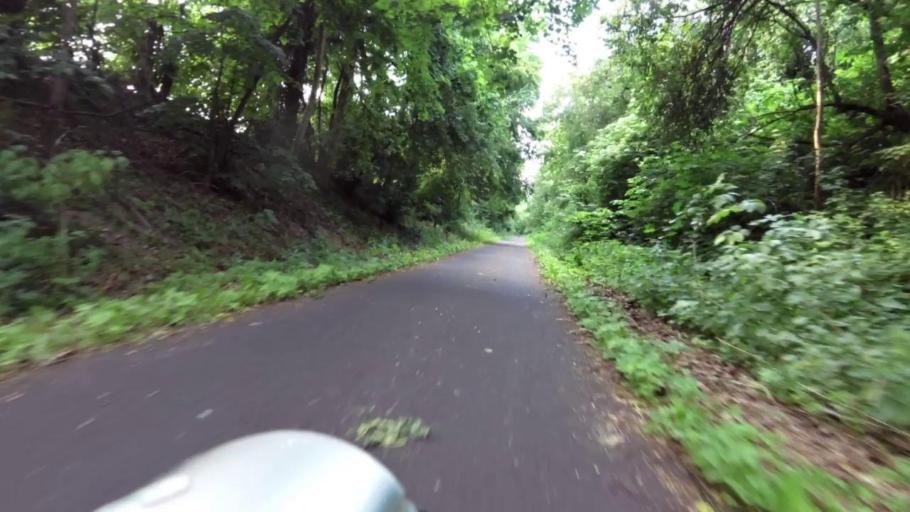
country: PL
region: Kujawsko-Pomorskie
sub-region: Powiat torunski
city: Lubianka
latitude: 53.0864
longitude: 18.5354
